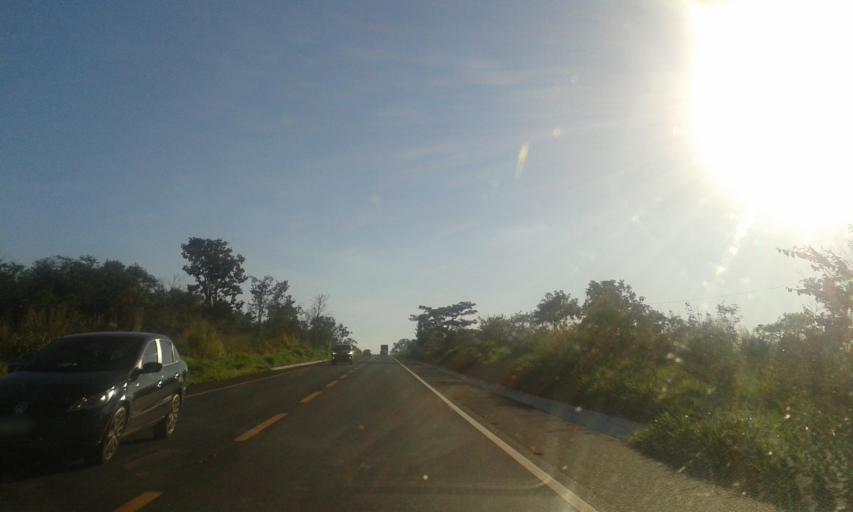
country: BR
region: Minas Gerais
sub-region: Monte Alegre De Minas
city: Monte Alegre de Minas
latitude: -18.8803
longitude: -49.1661
